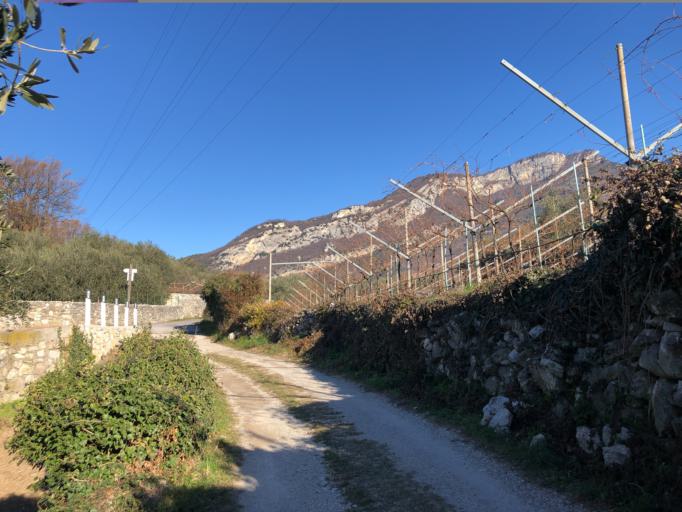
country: IT
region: Trentino-Alto Adige
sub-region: Provincia di Trento
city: Nago-Torbole
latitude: 45.8690
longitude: 10.8868
